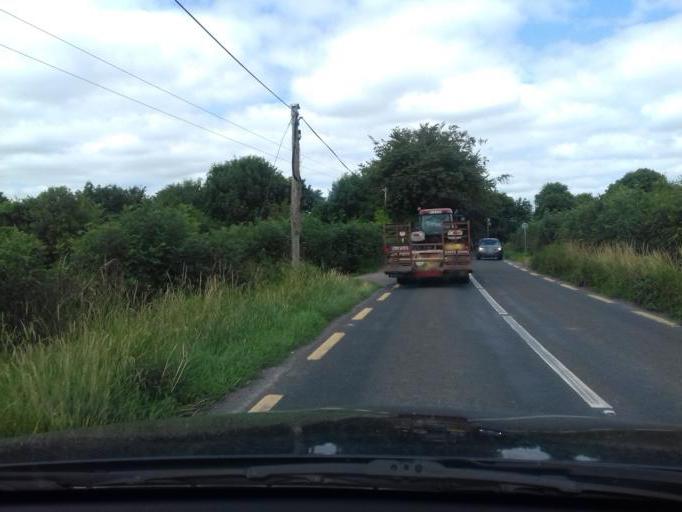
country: IE
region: Leinster
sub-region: County Carlow
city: Tullow
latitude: 52.8294
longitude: -6.7205
